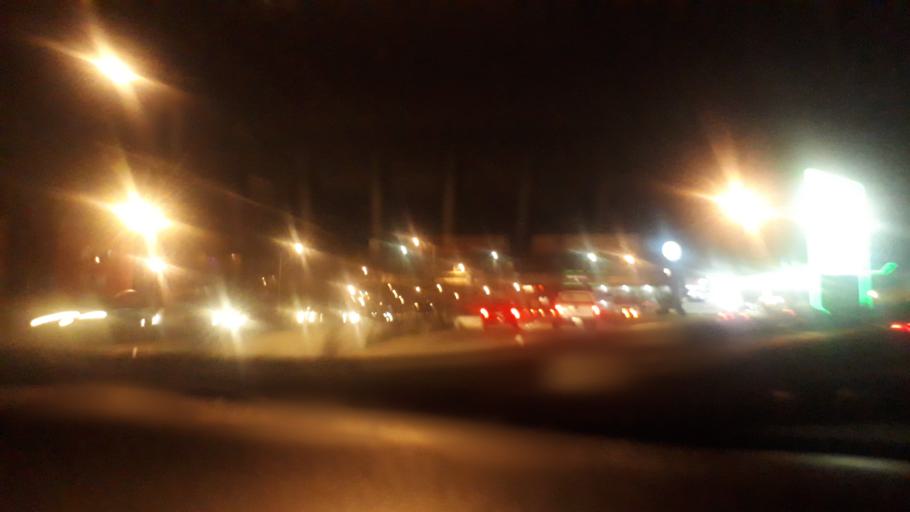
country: MX
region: Puebla
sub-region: Puebla
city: El Capulo (La Quebradora)
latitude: 18.9933
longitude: -98.2512
